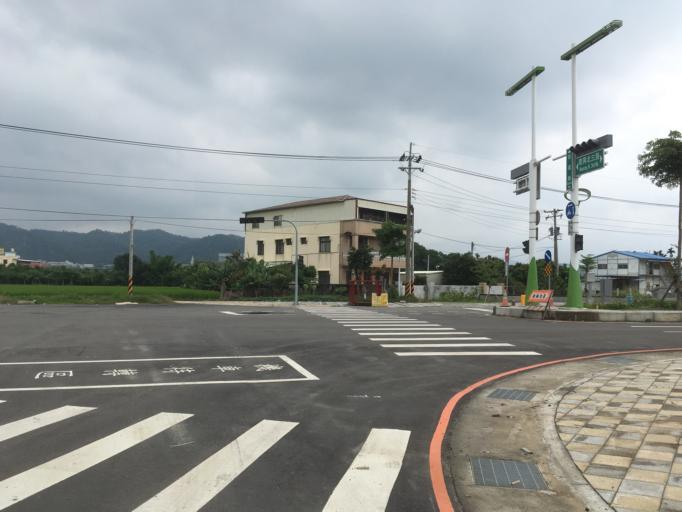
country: TW
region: Taiwan
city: Fengyuan
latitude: 24.1975
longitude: 120.7074
